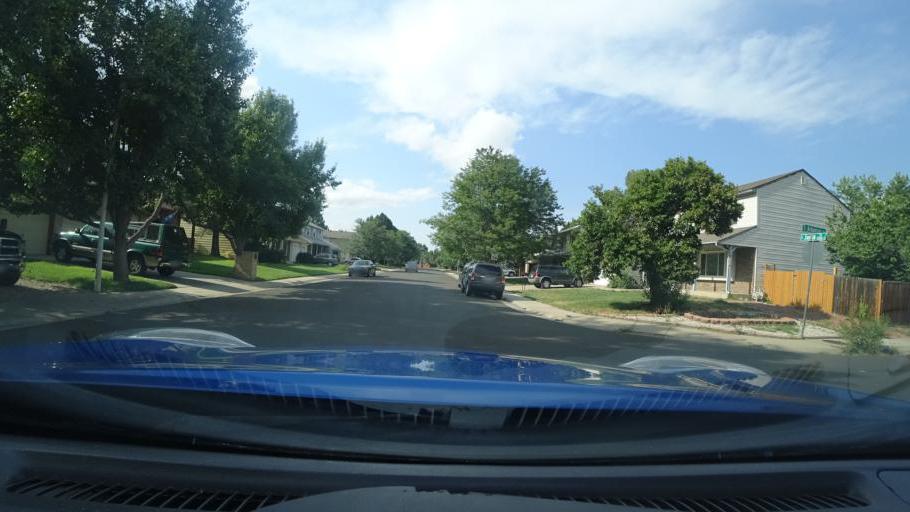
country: US
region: Colorado
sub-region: Adams County
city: Aurora
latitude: 39.6927
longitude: -104.8040
